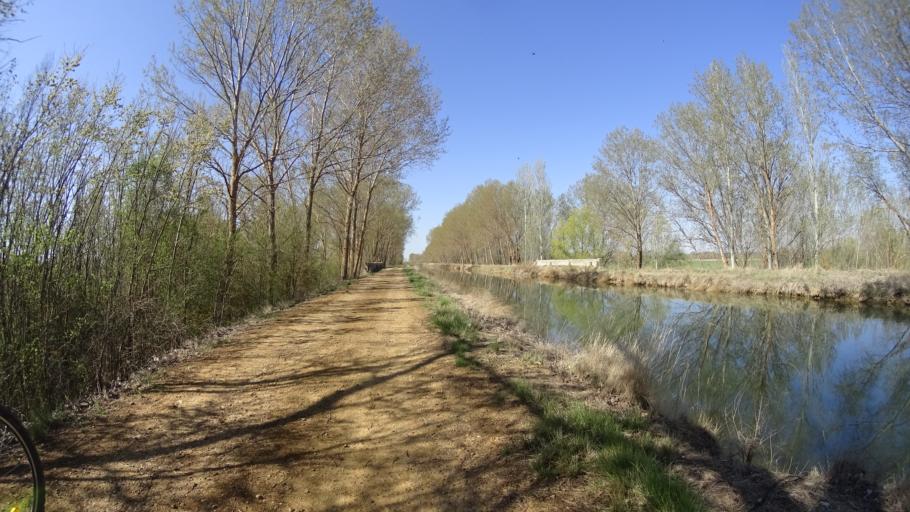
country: ES
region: Castille and Leon
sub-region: Provincia de Palencia
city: Fromista
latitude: 42.2462
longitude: -4.4246
